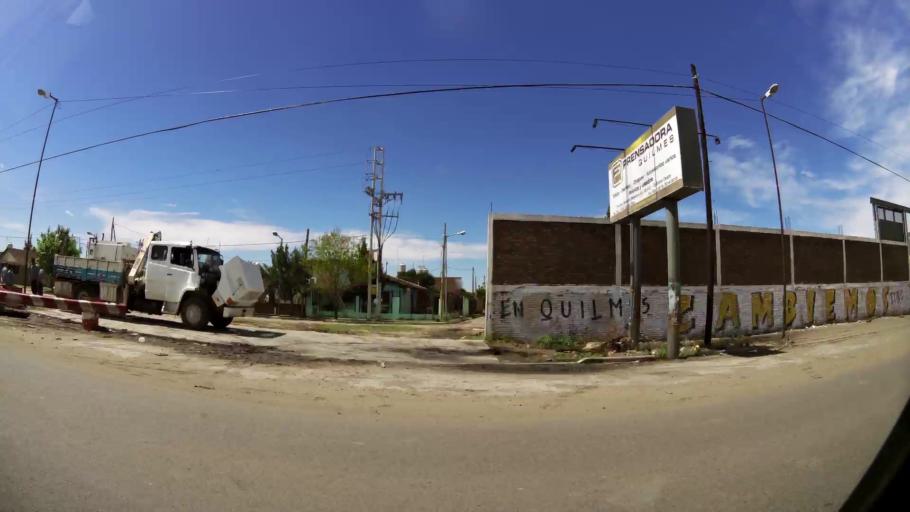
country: AR
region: Buenos Aires
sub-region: Partido de Quilmes
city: Quilmes
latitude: -34.7491
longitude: -58.3079
